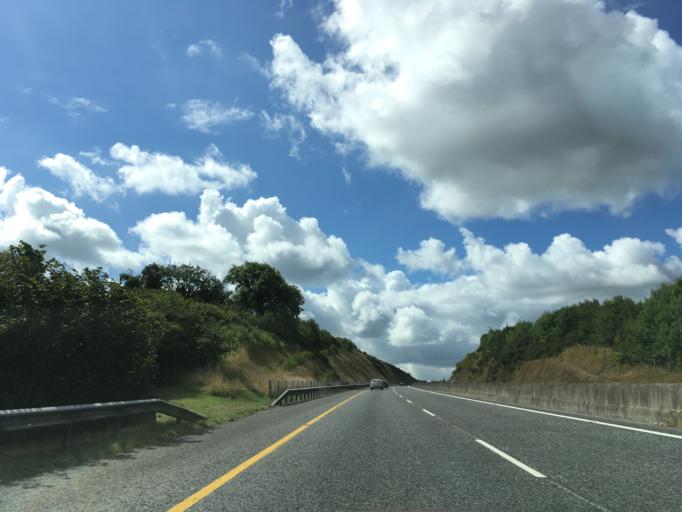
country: IE
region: Munster
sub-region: County Cork
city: Rathcormac
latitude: 52.0606
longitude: -8.3043
